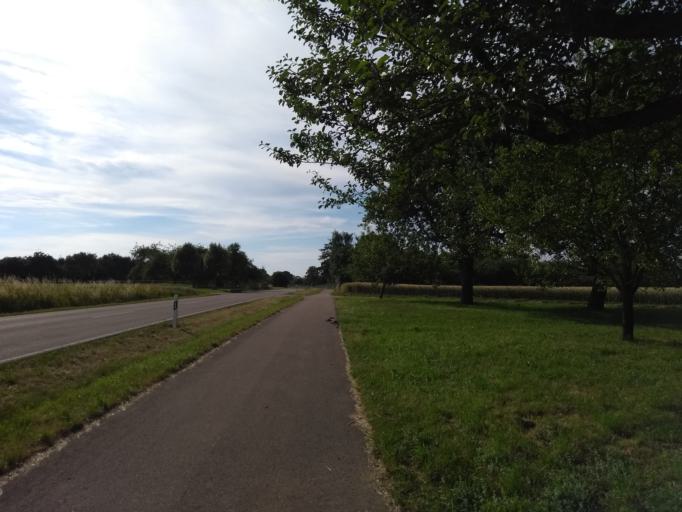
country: DE
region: Baden-Wuerttemberg
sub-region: Tuebingen Region
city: Blaubeuren
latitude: 48.4571
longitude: 9.8550
